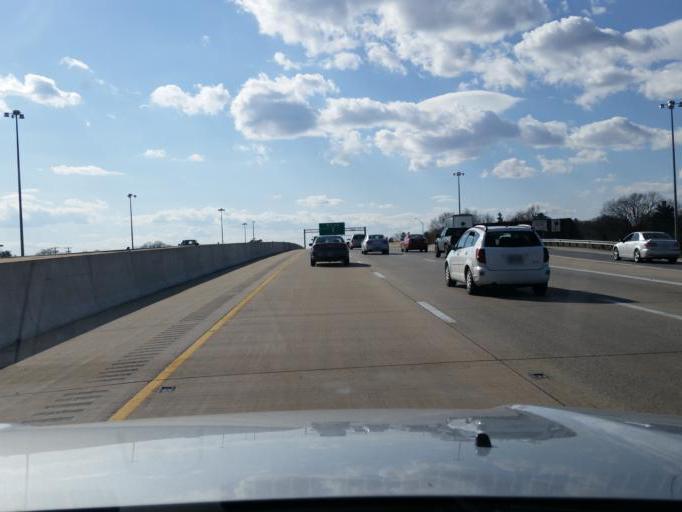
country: US
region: Pennsylvania
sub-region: Lancaster County
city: Lancaster
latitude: 40.0683
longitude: -76.3013
